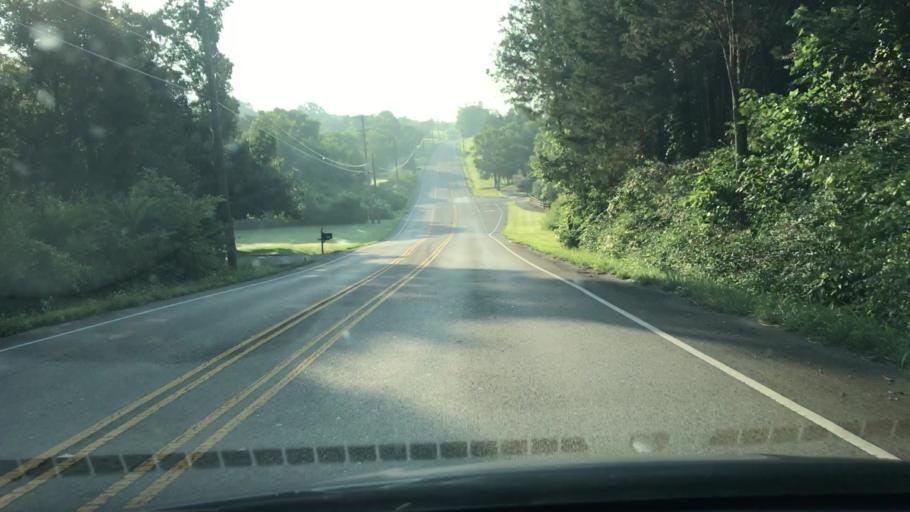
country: US
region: Tennessee
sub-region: Williamson County
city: Nolensville
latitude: 35.9911
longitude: -86.6772
